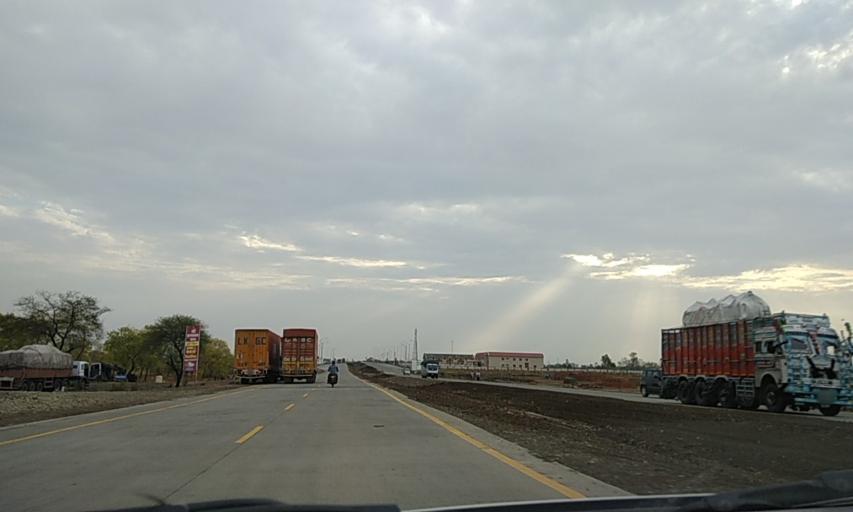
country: IN
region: Madhya Pradesh
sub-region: Rajgarh
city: Biaora
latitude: 23.8767
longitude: 76.8741
